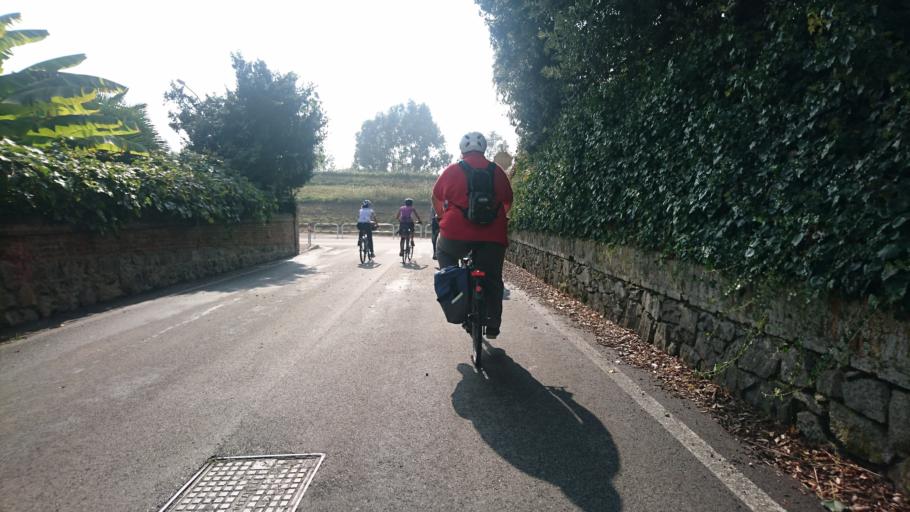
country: IT
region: Veneto
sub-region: Provincia di Padova
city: Boara Pisani
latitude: 45.1094
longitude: 11.7871
